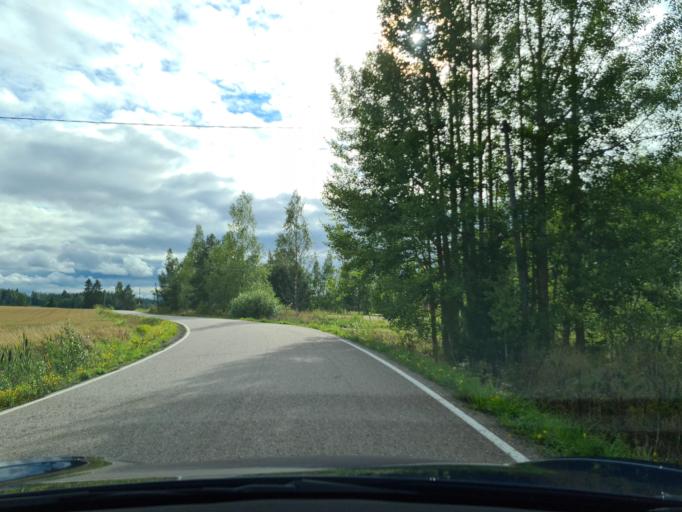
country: FI
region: Uusimaa
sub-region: Helsinki
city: Vihti
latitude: 60.4439
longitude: 24.3923
